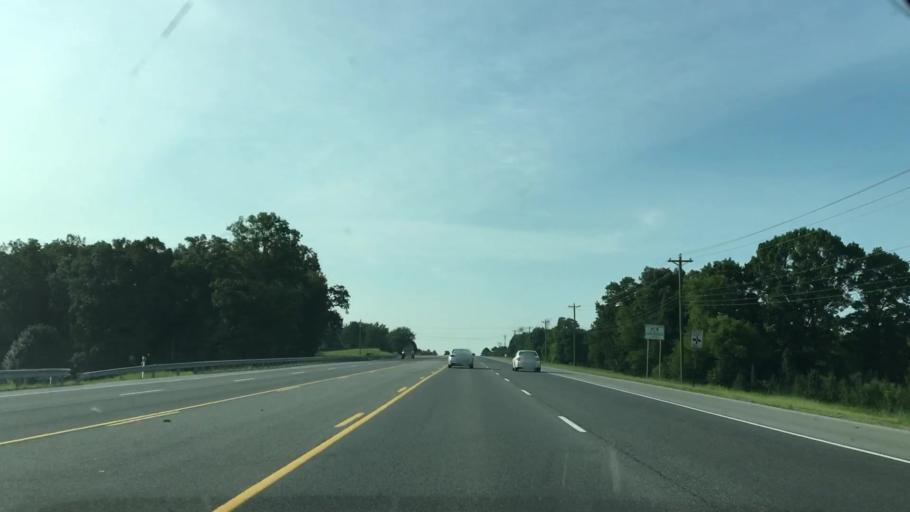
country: US
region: Tennessee
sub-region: Wilson County
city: Mount Juliet
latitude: 36.2152
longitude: -86.4224
